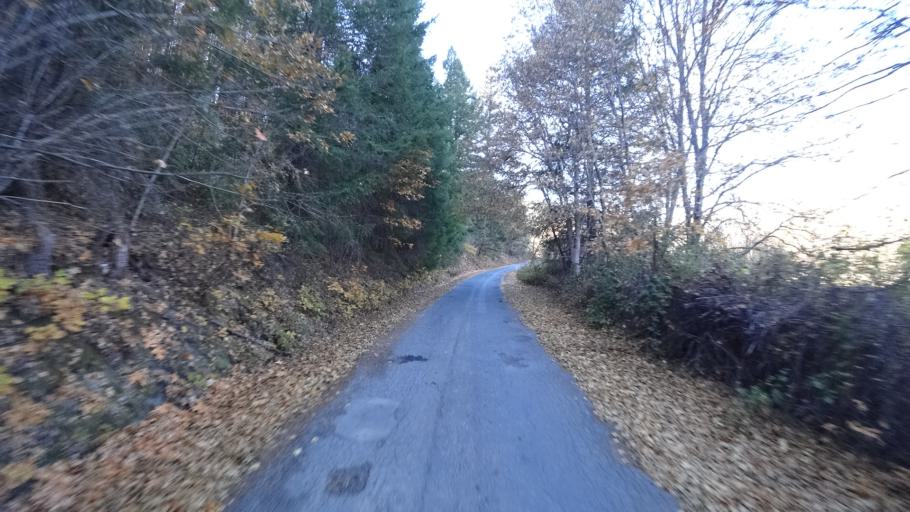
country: US
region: California
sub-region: Siskiyou County
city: Yreka
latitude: 41.8419
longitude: -122.8860
